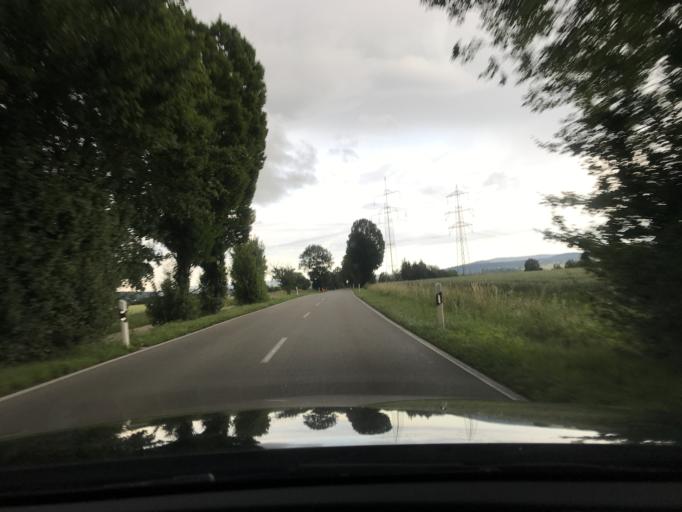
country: DE
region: Baden-Wuerttemberg
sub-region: Regierungsbezirk Stuttgart
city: Affalterbach
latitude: 48.8873
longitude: 9.2949
